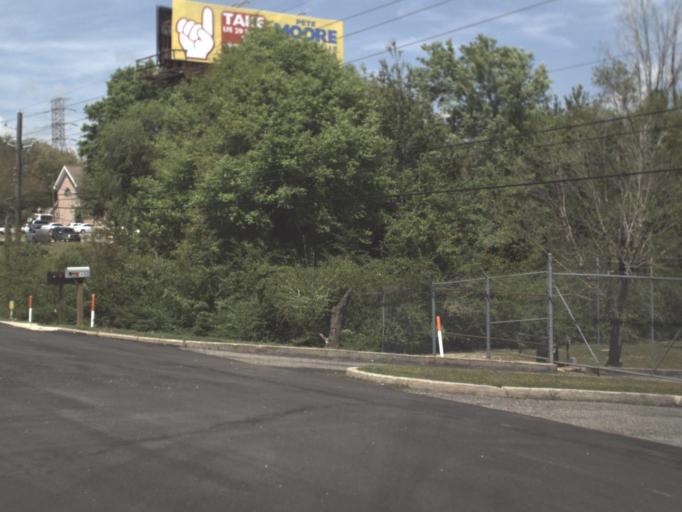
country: US
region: Florida
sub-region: Escambia County
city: Ferry Pass
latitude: 30.5326
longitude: -87.2341
